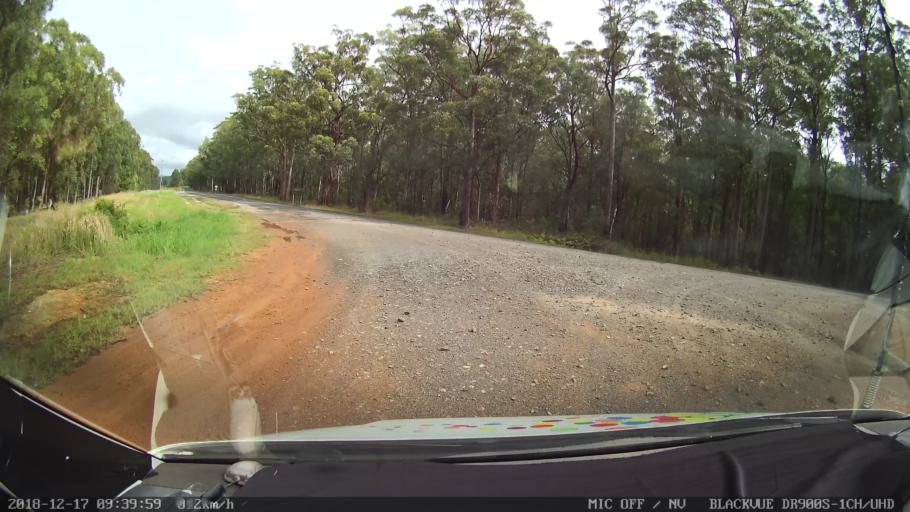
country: AU
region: New South Wales
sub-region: Tenterfield Municipality
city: Carrolls Creek
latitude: -28.9259
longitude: 152.3161
